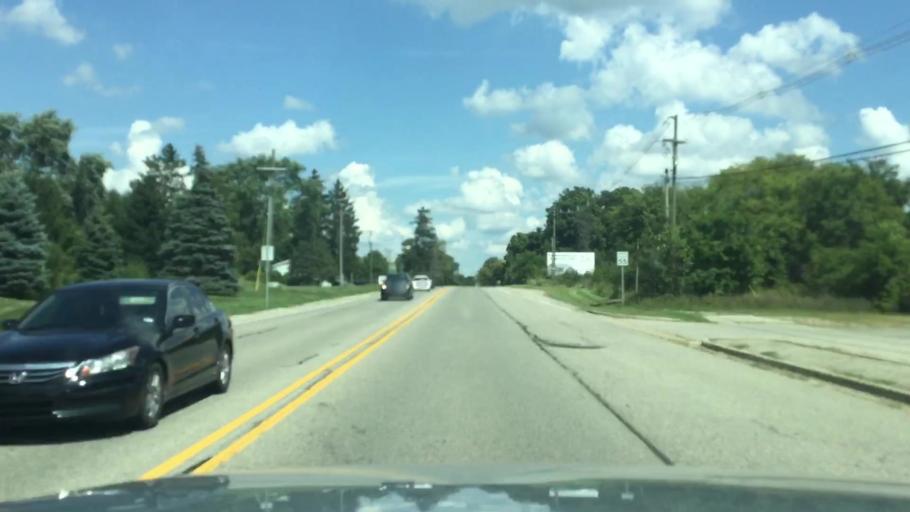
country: US
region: Michigan
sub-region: Lenawee County
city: Clinton
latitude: 42.0765
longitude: -83.9629
